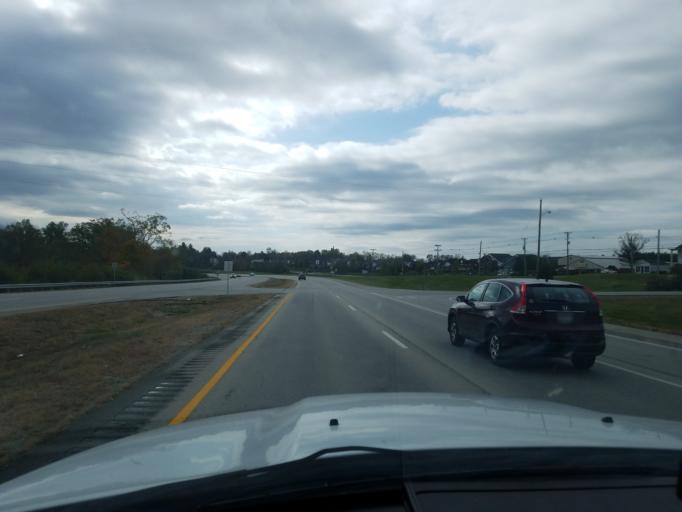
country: US
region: Kentucky
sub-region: Bullitt County
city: Mount Washington
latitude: 38.1011
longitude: -85.5657
